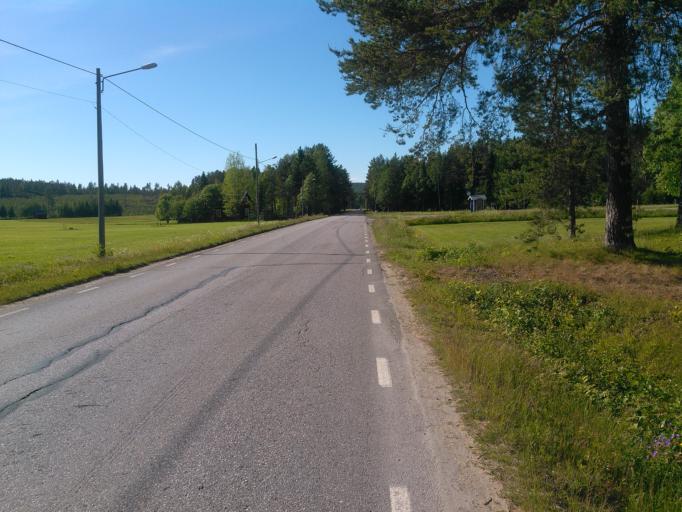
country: SE
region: Vaesterbotten
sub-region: Umea Kommun
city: Roback
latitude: 63.8298
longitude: 20.1140
